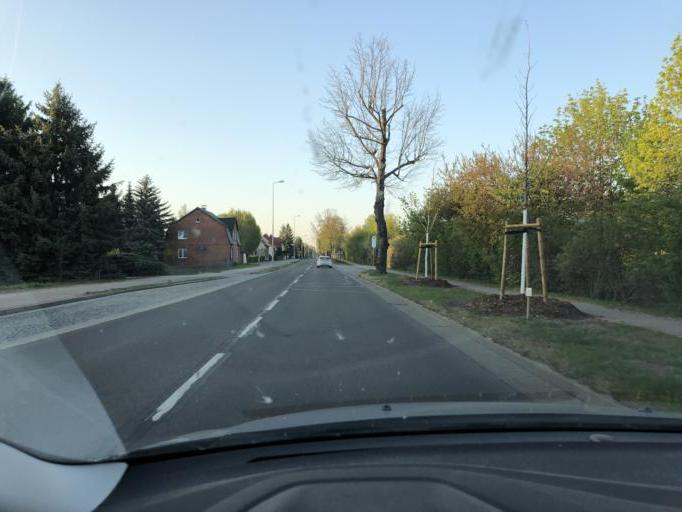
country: DE
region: Brandenburg
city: Spremberg
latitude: 51.5355
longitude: 14.3415
